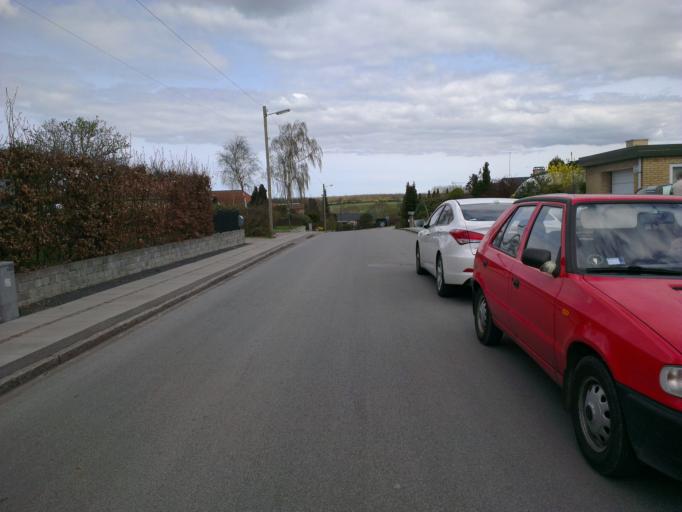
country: DK
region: Capital Region
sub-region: Frederikssund Kommune
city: Frederikssund
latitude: 55.8351
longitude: 12.0728
